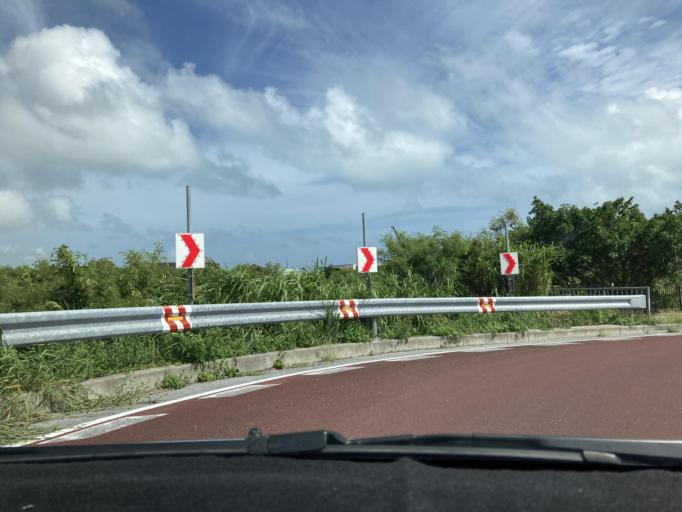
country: JP
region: Okinawa
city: Ginowan
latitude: 26.2180
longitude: 127.7734
